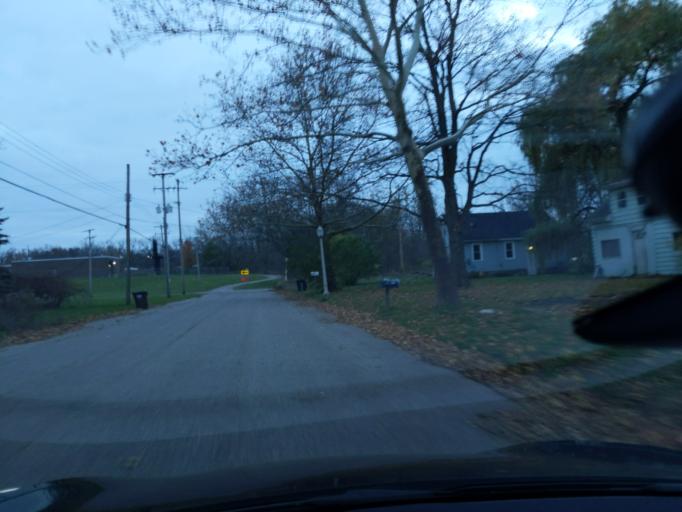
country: US
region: Michigan
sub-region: Ingham County
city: East Lansing
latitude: 42.7265
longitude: -84.5153
